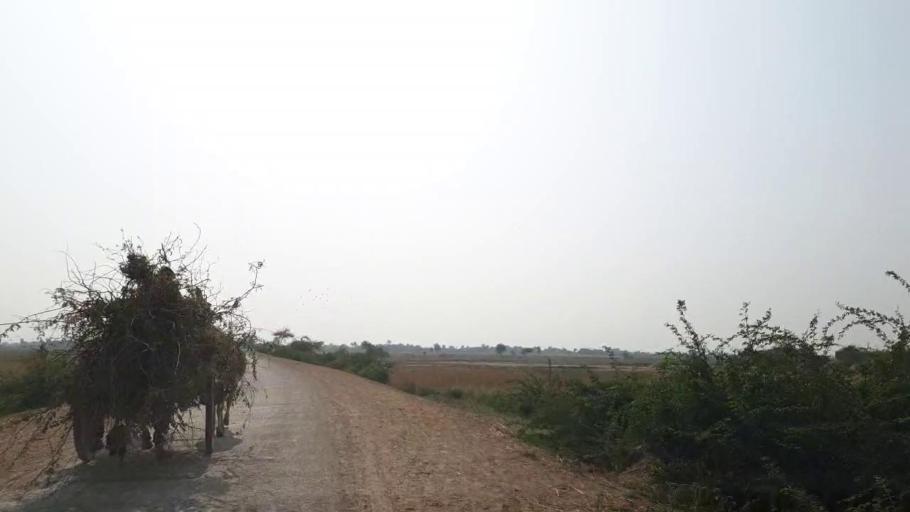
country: PK
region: Sindh
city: Matli
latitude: 24.9698
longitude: 68.5857
